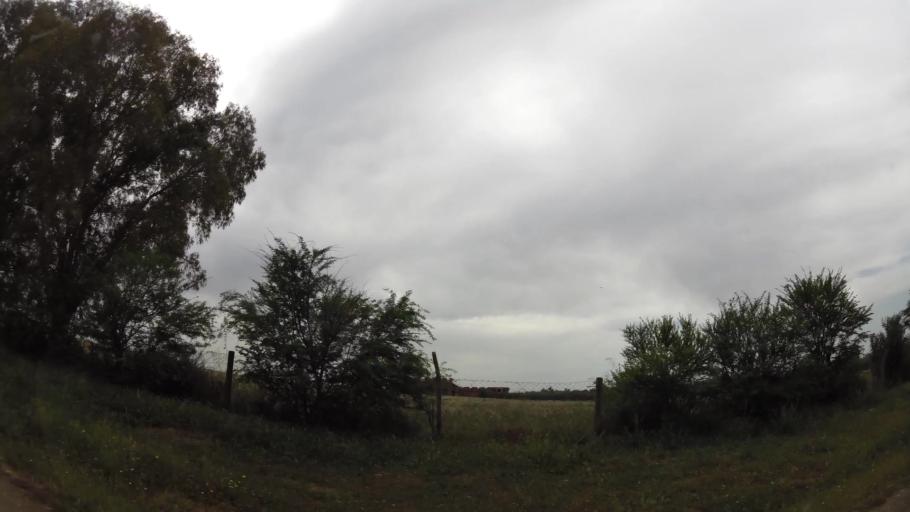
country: MA
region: Rabat-Sale-Zemmour-Zaer
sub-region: Khemisset
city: Tiflet
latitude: 33.8234
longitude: -6.2723
